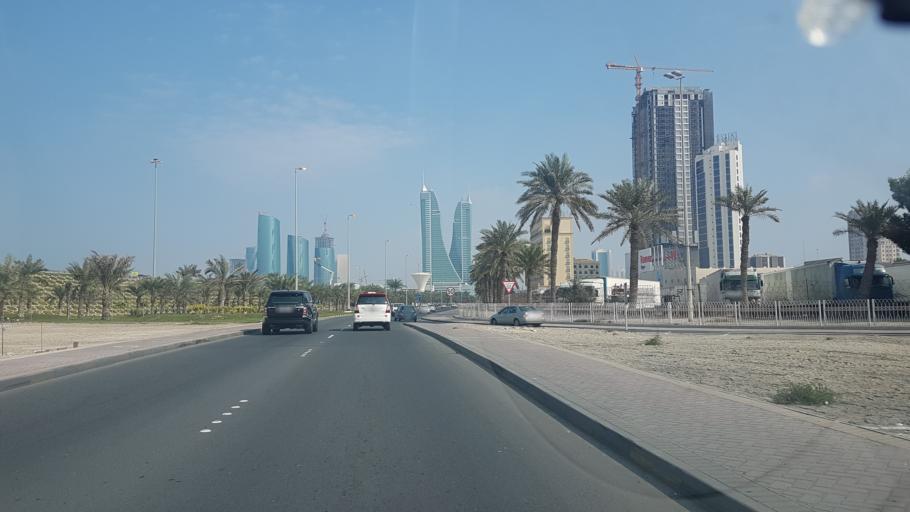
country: BH
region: Manama
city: Jidd Hafs
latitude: 26.2305
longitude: 50.5618
